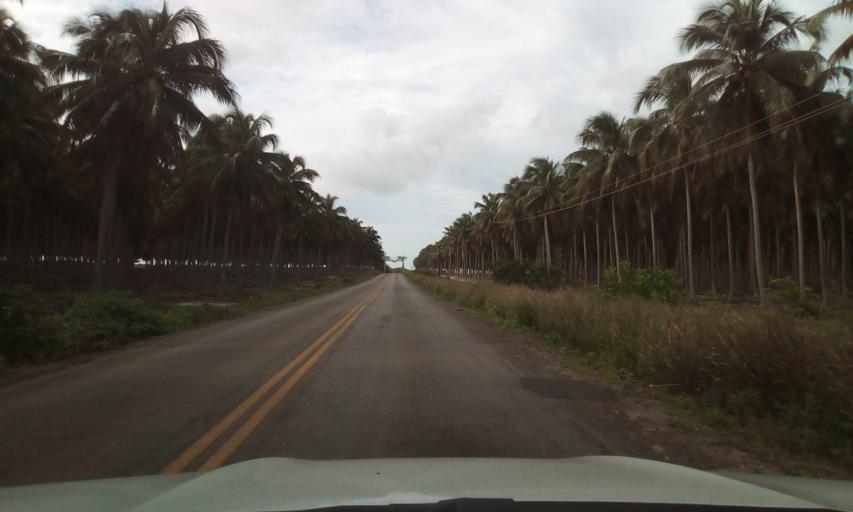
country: BR
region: Paraiba
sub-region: Cabedelo
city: Cabedelo
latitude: -6.9367
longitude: -34.9039
